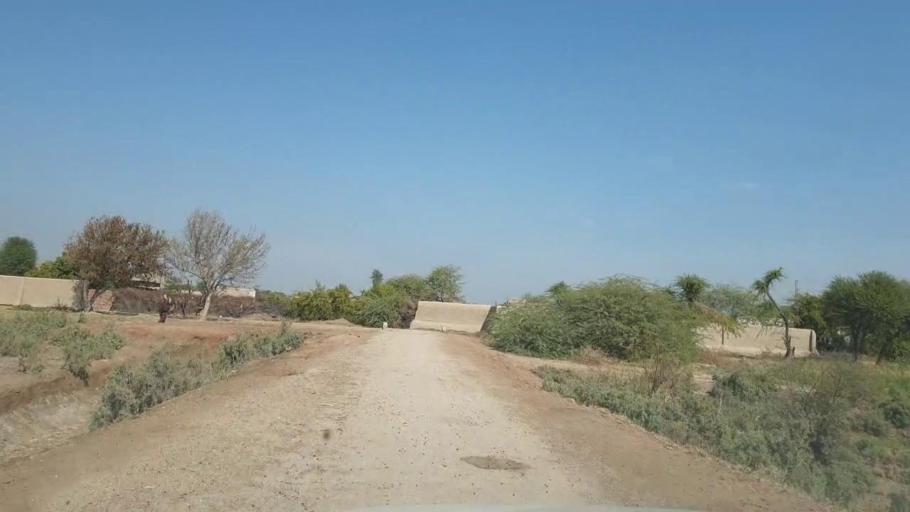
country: PK
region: Sindh
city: Mirpur Khas
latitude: 25.6308
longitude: 69.0954
